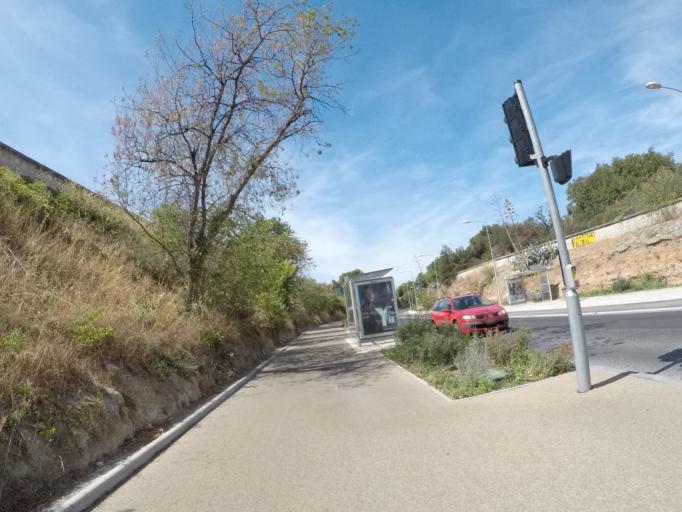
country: FR
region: Provence-Alpes-Cote d'Azur
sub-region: Departement des Bouches-du-Rhone
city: Marseille 09
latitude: 43.2454
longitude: 5.4117
